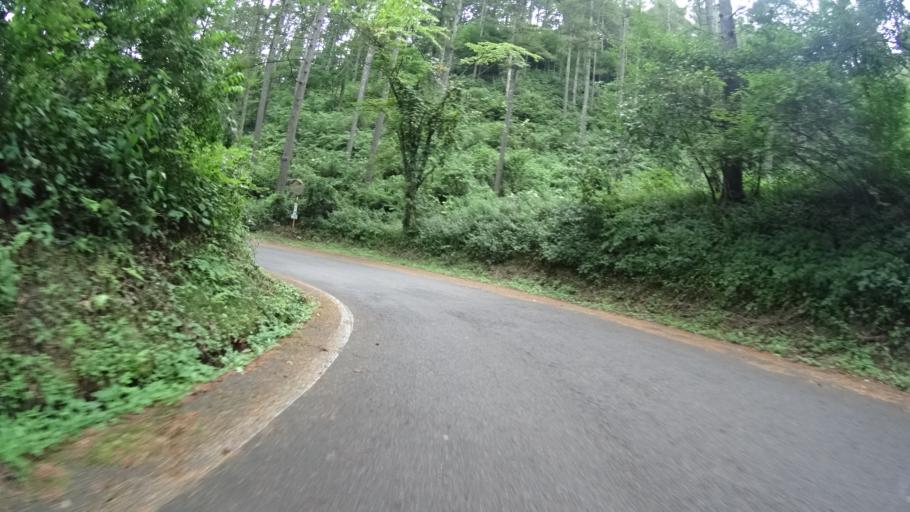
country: JP
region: Nagano
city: Saku
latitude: 36.0716
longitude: 138.6346
